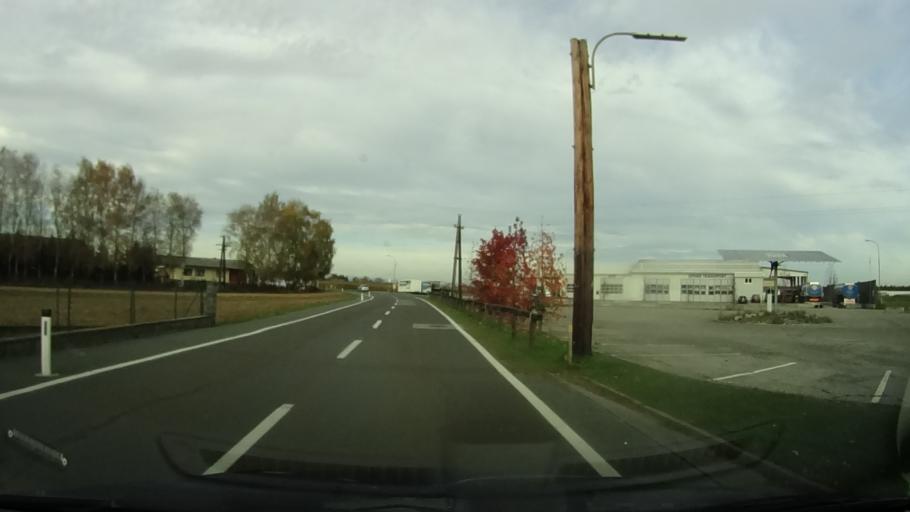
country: AT
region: Styria
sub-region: Politischer Bezirk Graz-Umgebung
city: Wundschuh
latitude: 46.9402
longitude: 15.4451
